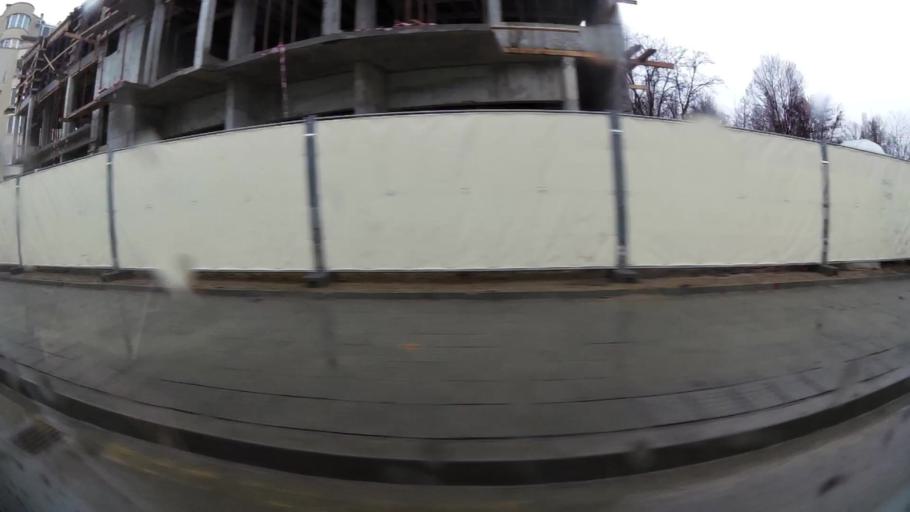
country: BG
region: Sofia-Capital
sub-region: Stolichna Obshtina
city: Sofia
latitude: 42.6596
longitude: 23.3625
